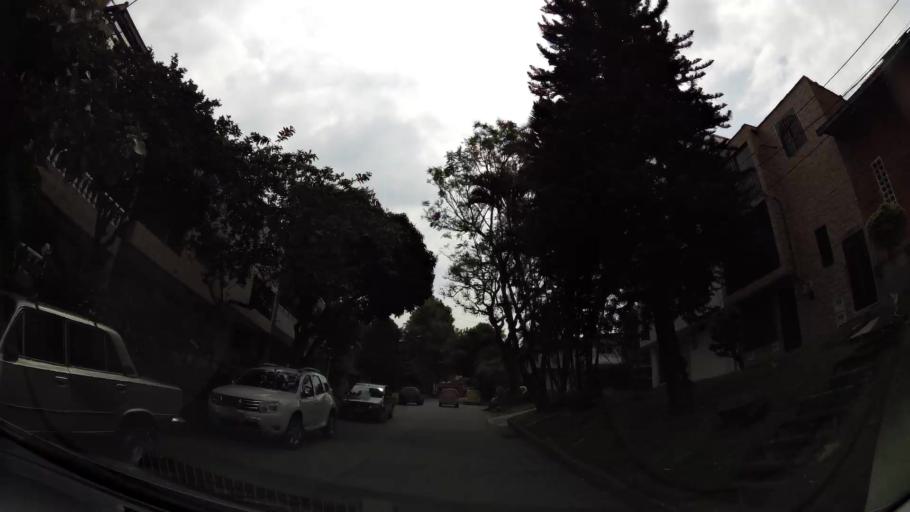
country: CO
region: Antioquia
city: Medellin
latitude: 6.2332
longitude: -75.5450
